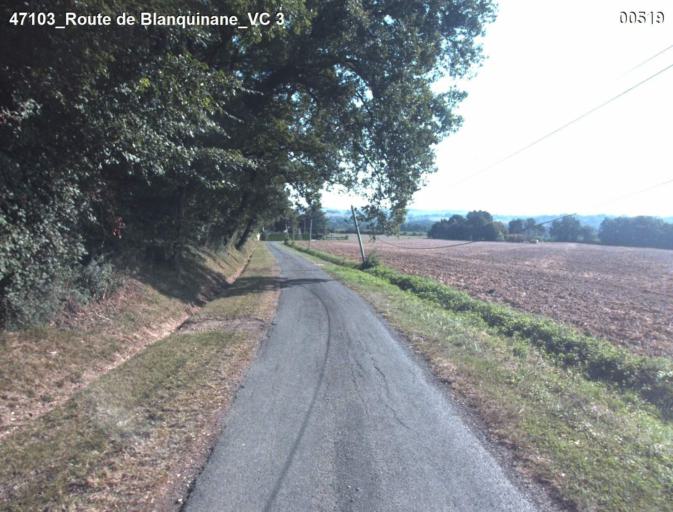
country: FR
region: Aquitaine
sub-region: Departement du Lot-et-Garonne
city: Nerac
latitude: 44.0837
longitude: 0.3579
